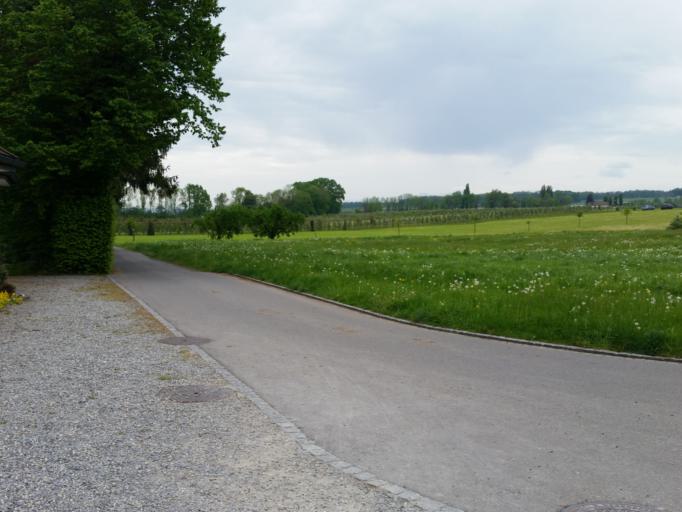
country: CH
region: Thurgau
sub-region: Kreuzlingen District
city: Guttingen
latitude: 47.6089
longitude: 9.3007
